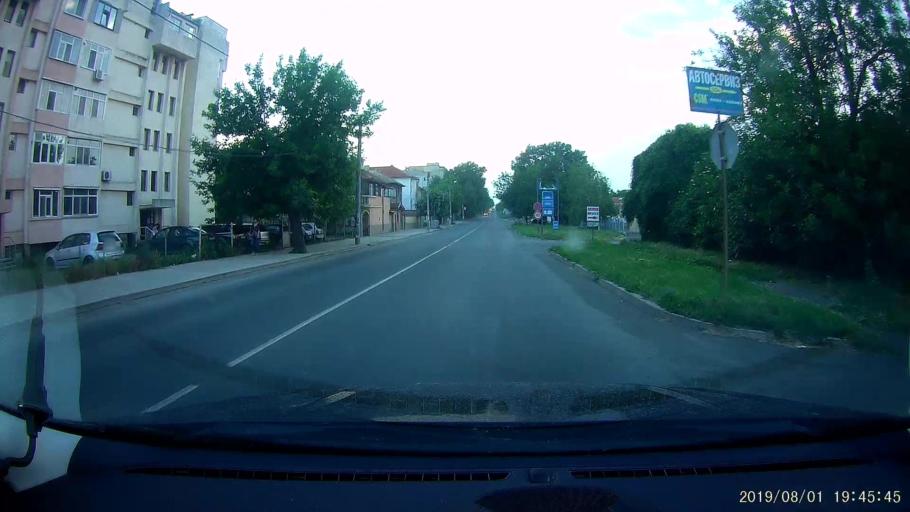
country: BG
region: Burgas
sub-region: Obshtina Karnobat
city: Karnobat
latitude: 42.6510
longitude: 26.9796
